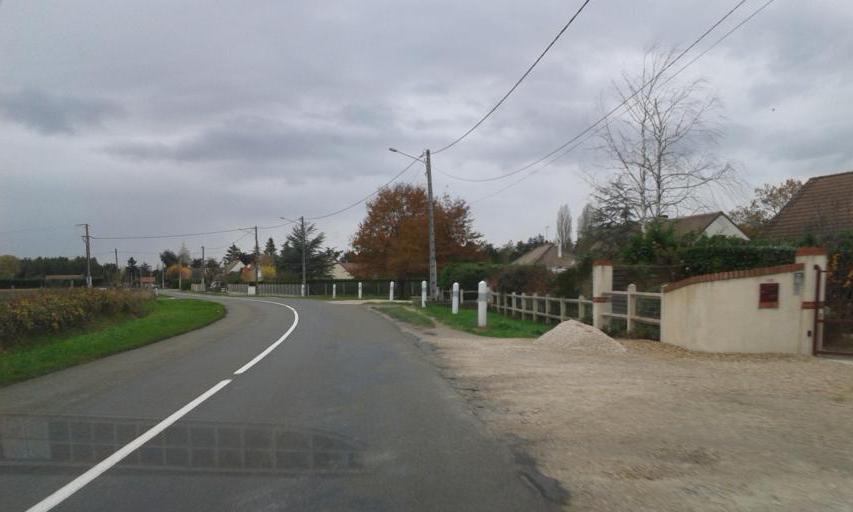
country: FR
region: Centre
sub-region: Departement du Loiret
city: Vitry-aux-Loges
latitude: 47.9340
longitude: 2.2516
